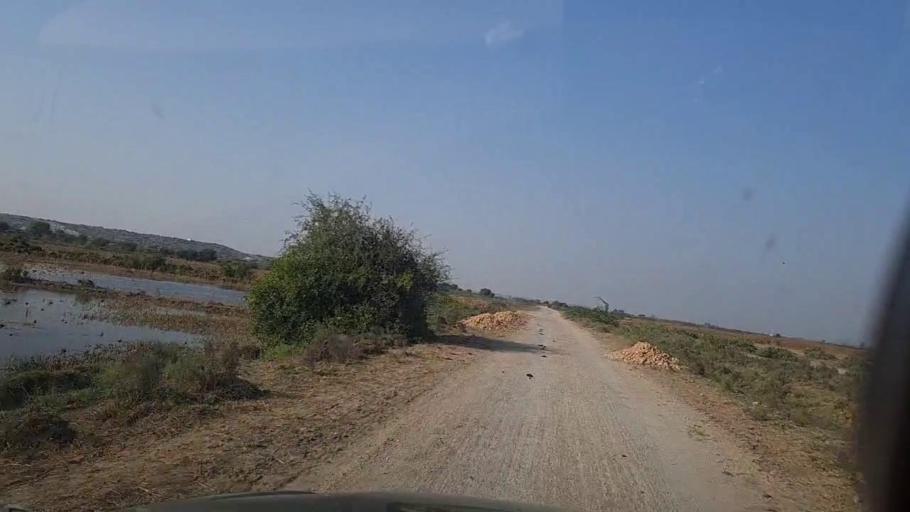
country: PK
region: Sindh
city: Thatta
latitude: 24.5895
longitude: 67.8763
